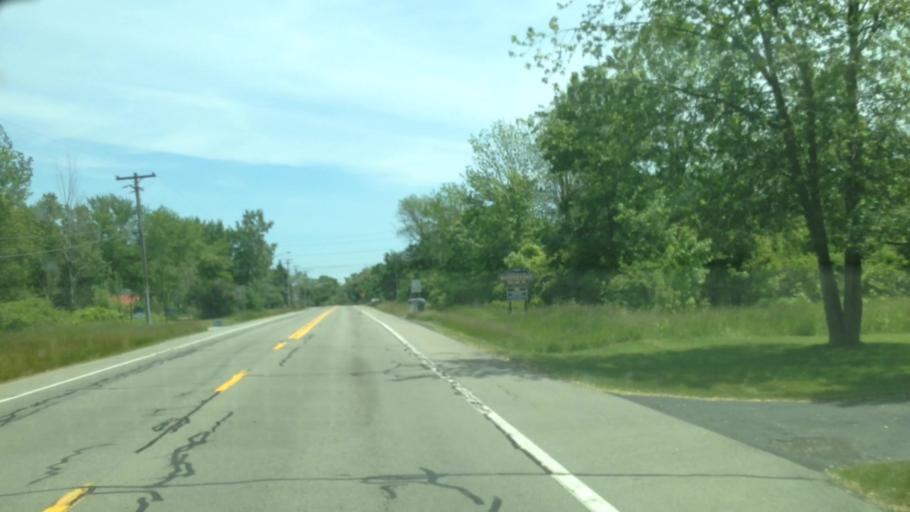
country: US
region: New York
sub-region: Niagara County
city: Wilson
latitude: 43.3062
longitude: -78.8651
